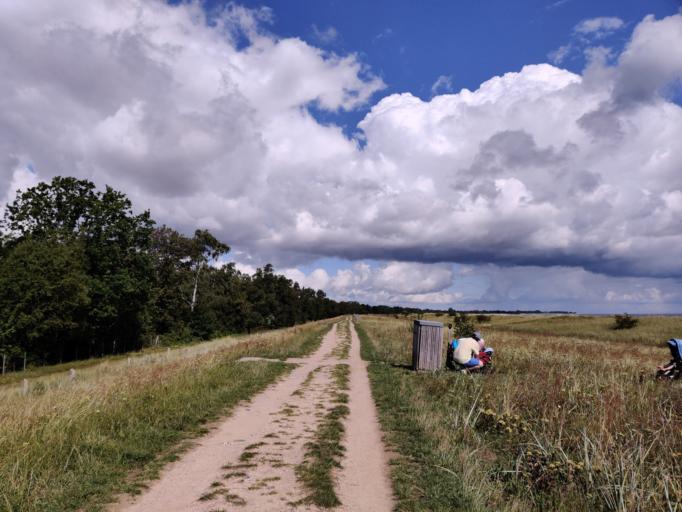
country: DK
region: Zealand
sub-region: Guldborgsund Kommune
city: Nykobing Falster
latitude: 54.6918
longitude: 11.9703
